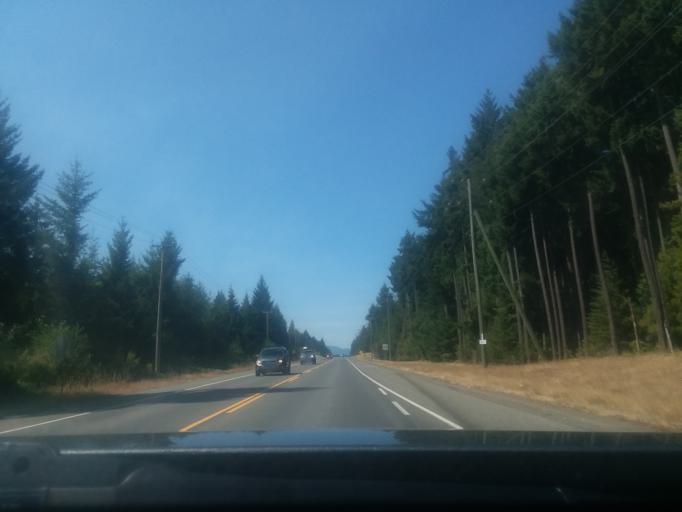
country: CA
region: British Columbia
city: Courtenay
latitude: 49.7152
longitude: -124.9368
